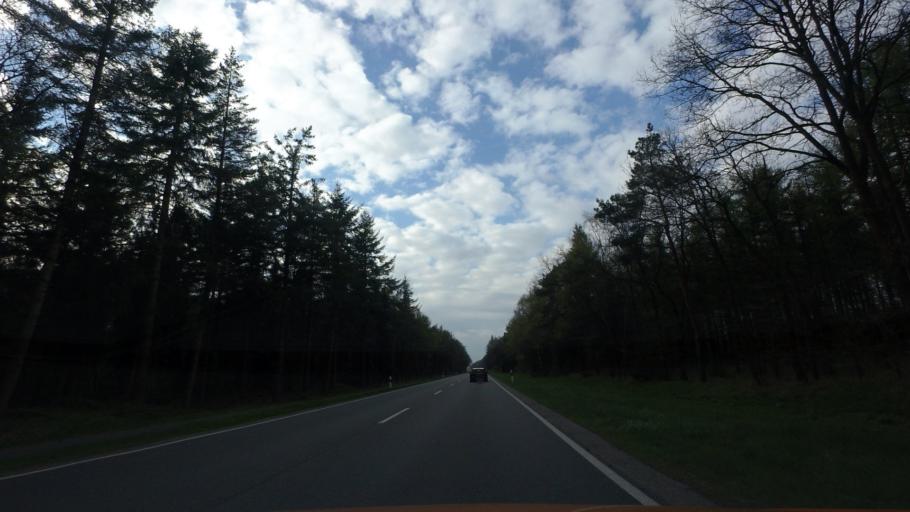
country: DE
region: Lower Saxony
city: Bosel
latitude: 52.9696
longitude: 7.9159
